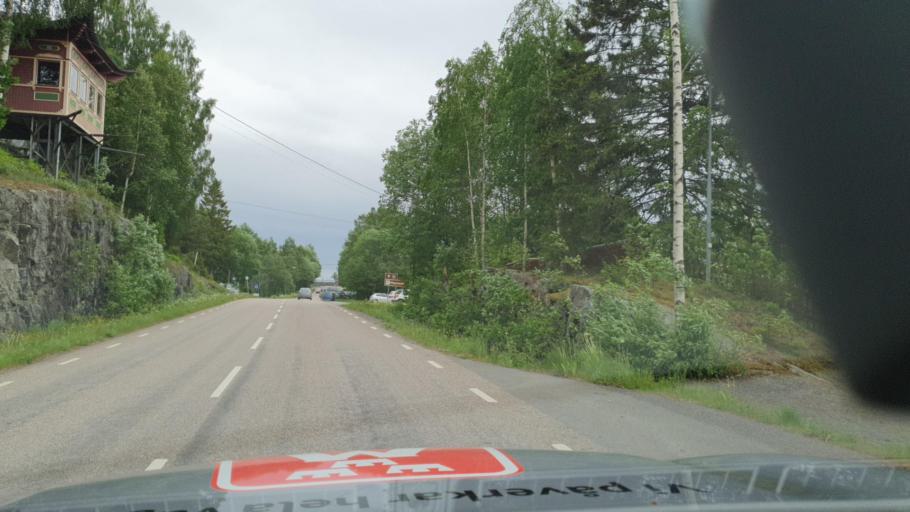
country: SE
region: Vaesternorrland
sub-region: Kramfors Kommun
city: Nordingra
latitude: 62.9113
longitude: 18.3014
